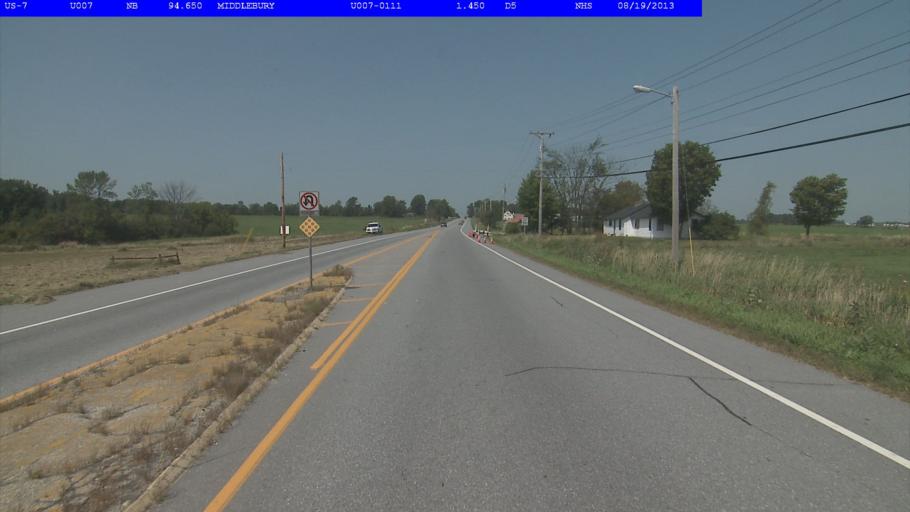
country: US
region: Vermont
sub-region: Addison County
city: Middlebury (village)
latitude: 43.9766
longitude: -73.1185
